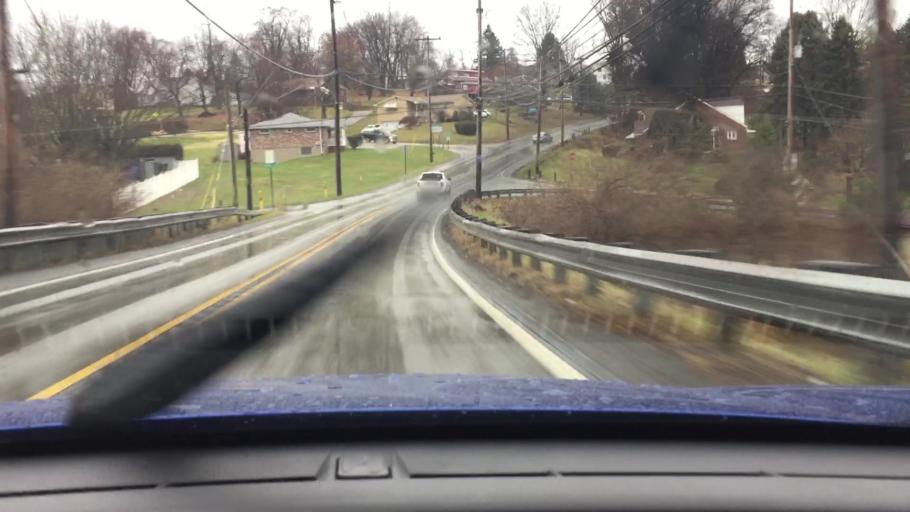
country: US
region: Pennsylvania
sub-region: Allegheny County
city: Jefferson Hills
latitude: 40.3218
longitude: -79.9255
